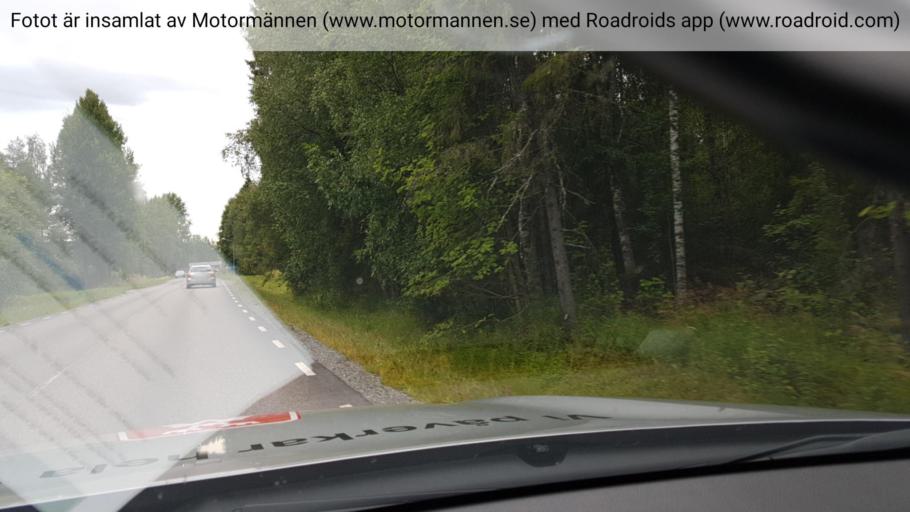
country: SE
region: Norrbotten
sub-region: Lulea Kommun
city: Gammelstad
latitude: 65.6510
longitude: 22.0320
